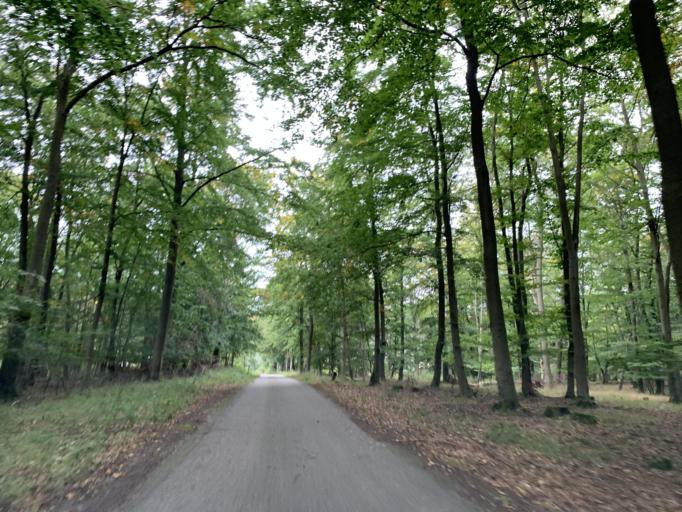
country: DE
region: Mecklenburg-Vorpommern
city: Woldegk
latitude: 53.3244
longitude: 13.6055
